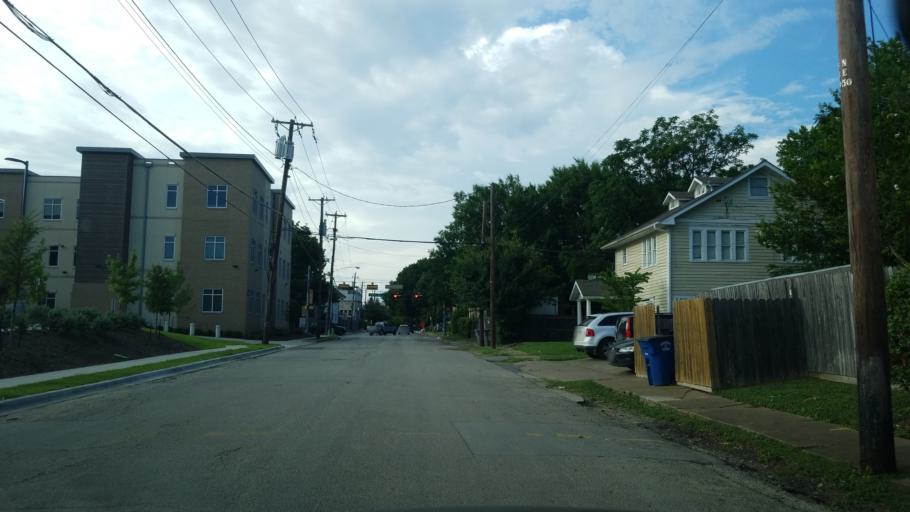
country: US
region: Texas
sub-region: Dallas County
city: Highland Park
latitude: 32.8103
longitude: -96.7685
